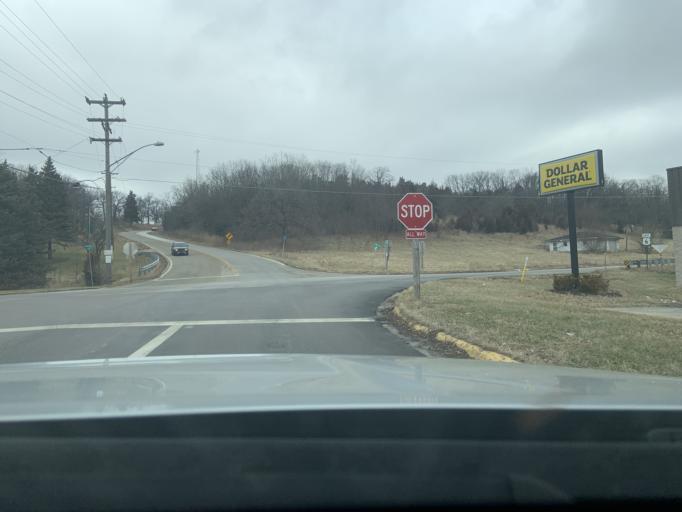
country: US
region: Illinois
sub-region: LaSalle County
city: Seneca
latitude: 41.3207
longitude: -88.6103
